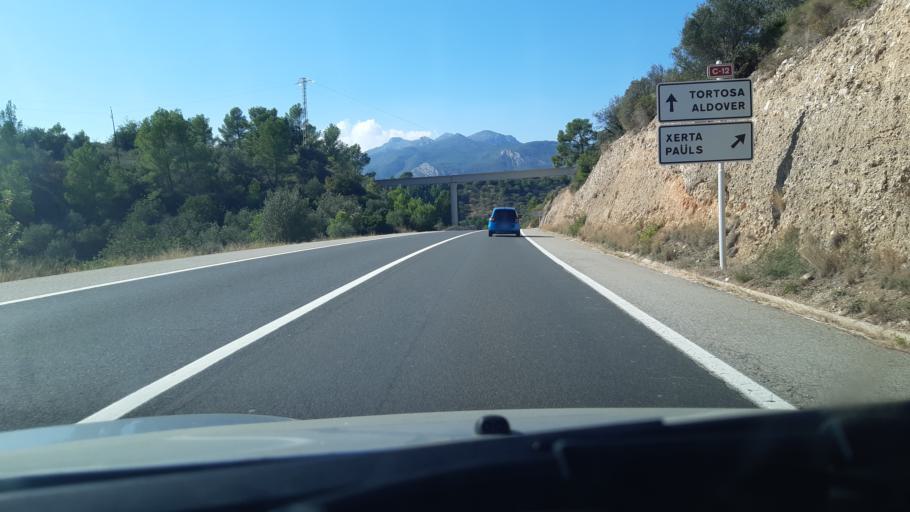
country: ES
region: Catalonia
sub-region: Provincia de Tarragona
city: Tivenys
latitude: 40.9140
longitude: 0.4902
